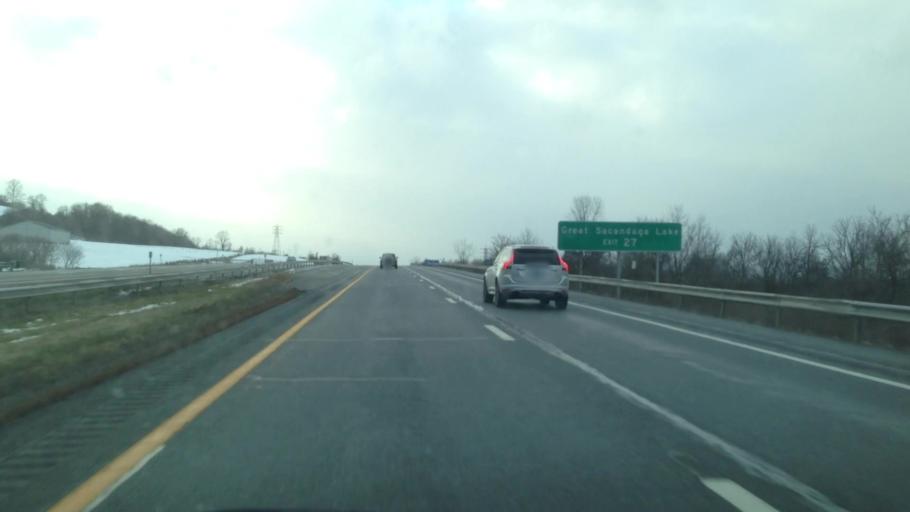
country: US
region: New York
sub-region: Montgomery County
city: Amsterdam
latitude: 42.9183
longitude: -74.1745
